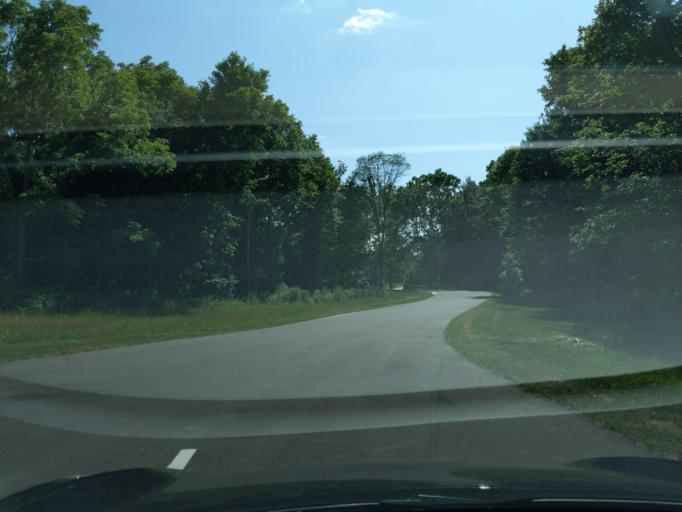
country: US
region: Michigan
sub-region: Eaton County
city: Grand Ledge
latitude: 42.7562
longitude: -84.7100
